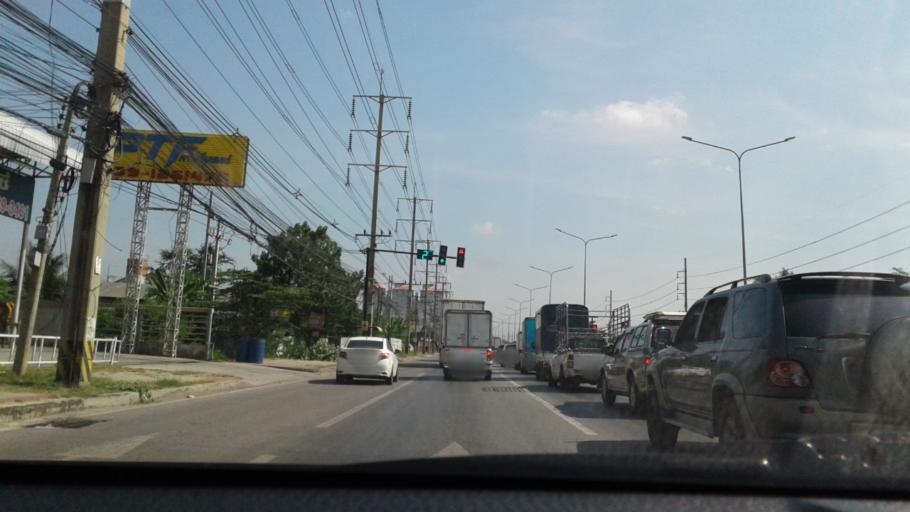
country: TH
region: Phra Nakhon Si Ayutthaya
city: Ban Bang Kadi Pathum Thani
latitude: 13.9767
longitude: 100.5844
